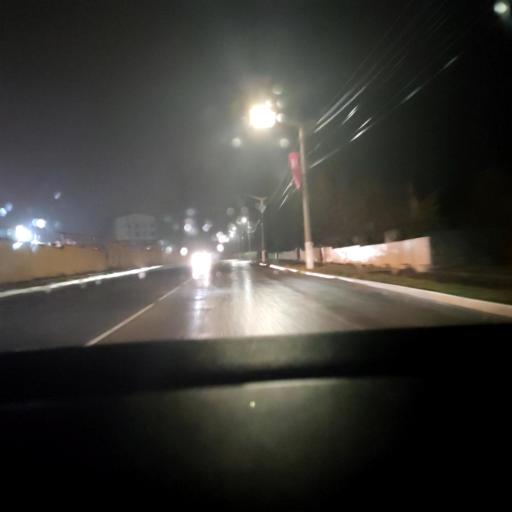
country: RU
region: Voronezj
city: Semiluki
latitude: 51.6877
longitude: 39.0390
